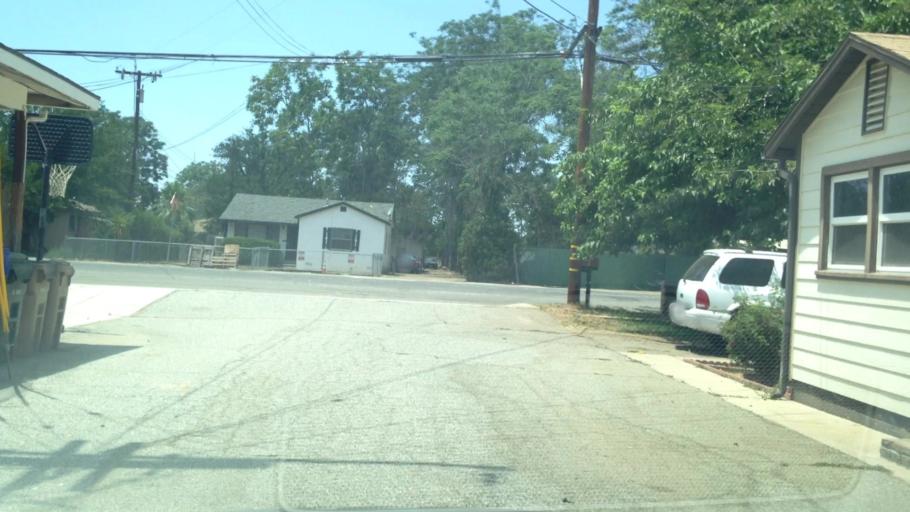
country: US
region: California
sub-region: Riverside County
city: Calimesa
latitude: 34.0275
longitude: -117.0951
